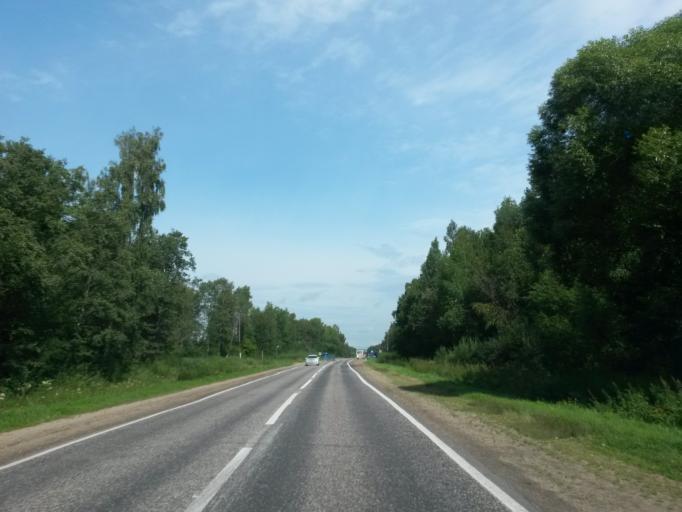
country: RU
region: Jaroslavl
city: Yaroslavl
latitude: 57.4900
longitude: 39.9015
